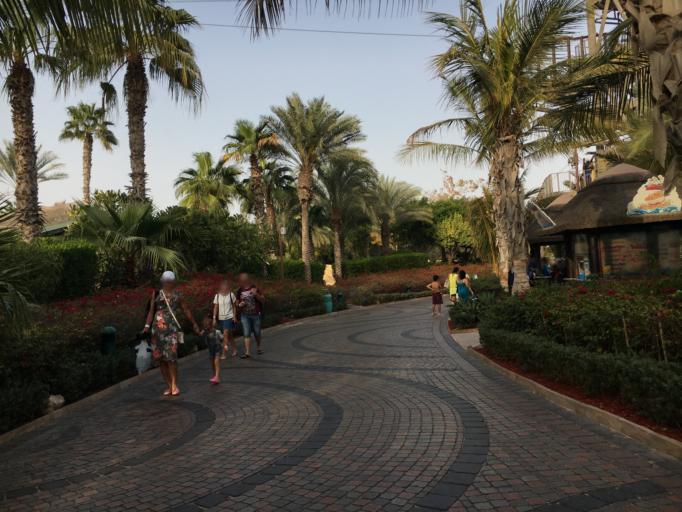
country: AE
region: Dubai
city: Dubai
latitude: 25.1336
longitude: 55.1212
